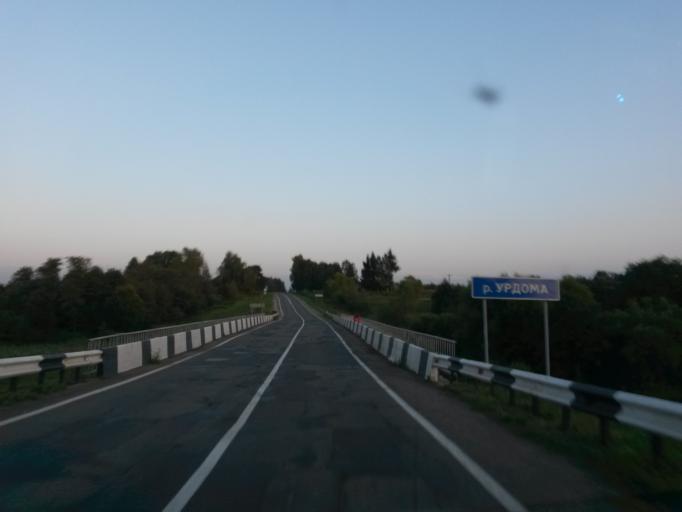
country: RU
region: Jaroslavl
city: Tutayev
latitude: 57.9419
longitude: 39.4959
